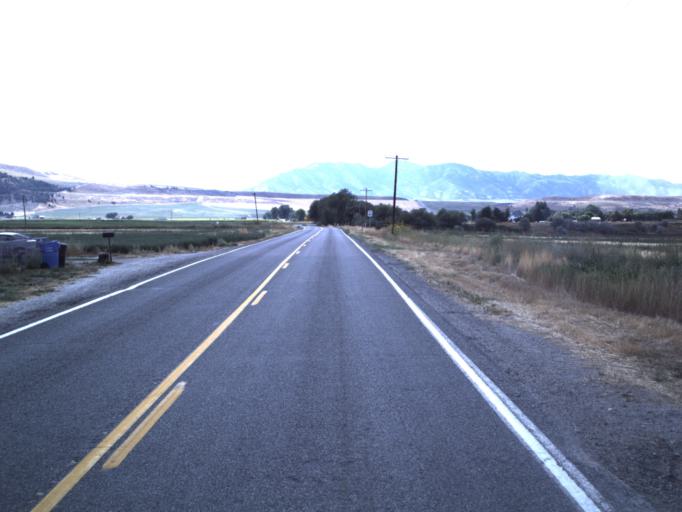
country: US
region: Utah
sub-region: Cache County
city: Lewiston
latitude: 41.9147
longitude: -111.9242
